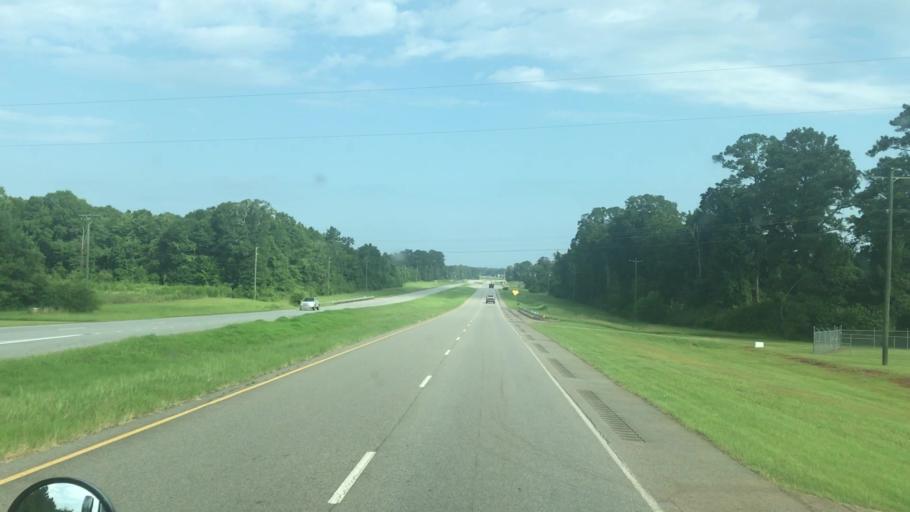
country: US
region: Georgia
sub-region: Early County
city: Blakely
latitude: 31.3462
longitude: -84.9116
